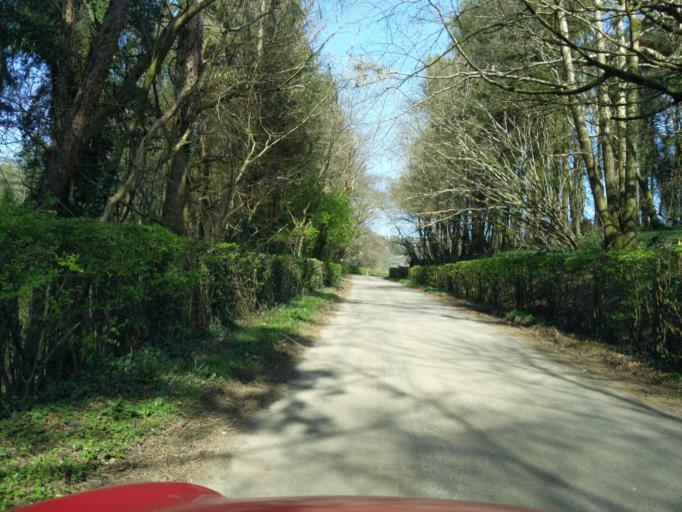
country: GB
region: England
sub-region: Devon
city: Bere Alston
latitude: 50.4631
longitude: -4.1378
